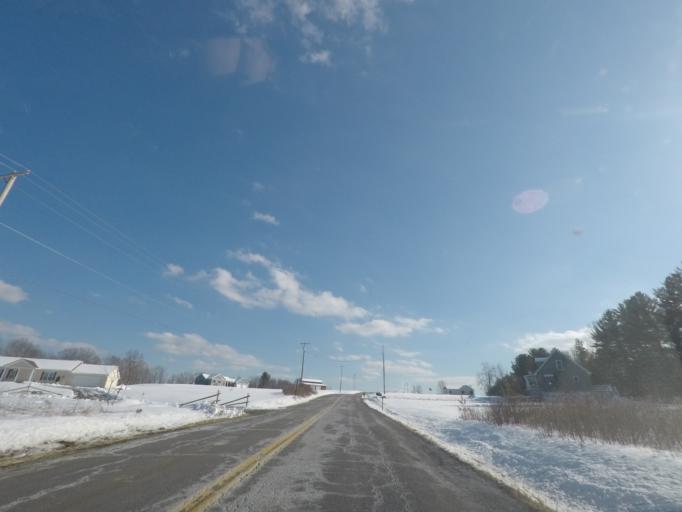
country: US
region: New York
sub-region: Rensselaer County
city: Hoosick Falls
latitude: 42.8466
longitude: -73.4897
